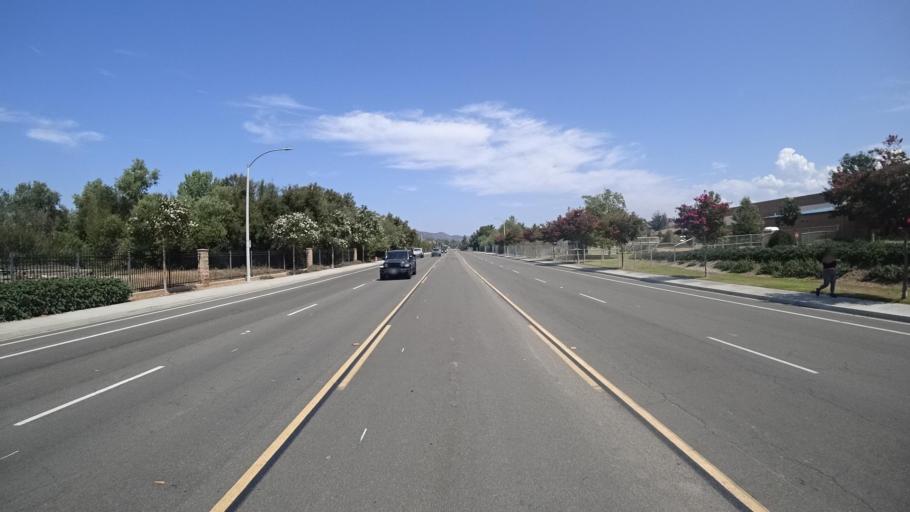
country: US
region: California
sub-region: San Diego County
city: Escondido
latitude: 33.1545
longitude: -117.0919
